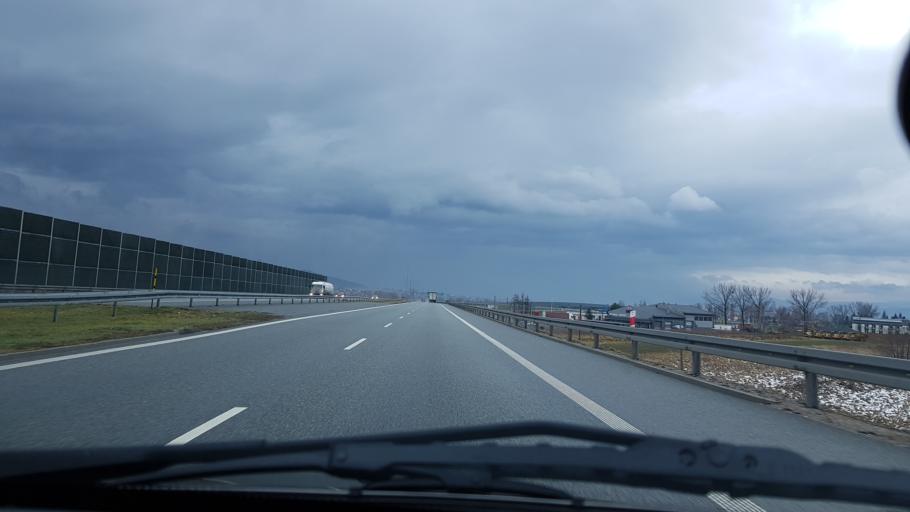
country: PL
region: Silesian Voivodeship
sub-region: Powiat bielski
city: Rybarzowice
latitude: 49.7416
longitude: 19.0977
